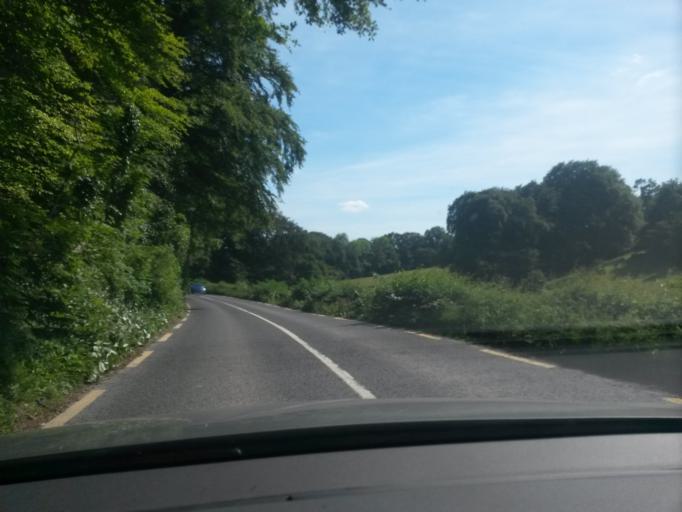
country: IE
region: Leinster
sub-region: Kildare
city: Eadestown
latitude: 53.1786
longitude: -6.5619
